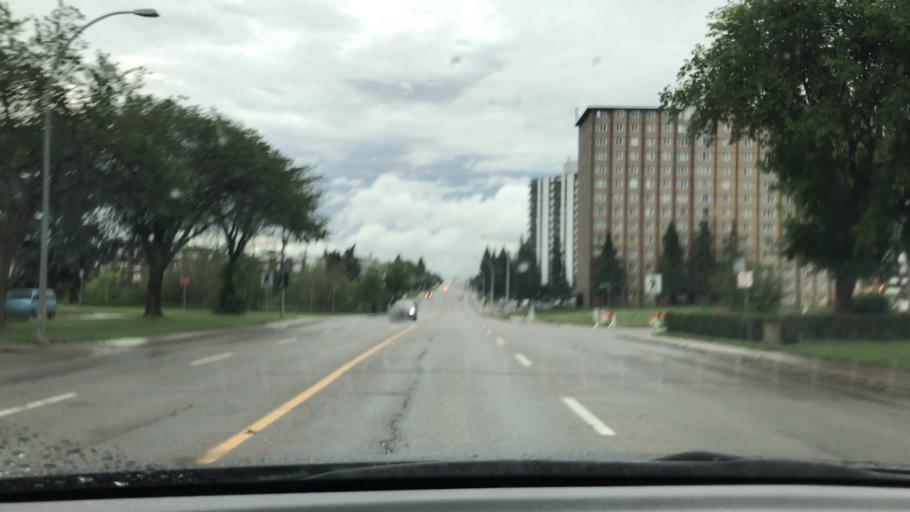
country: CA
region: Alberta
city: Edmonton
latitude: 53.5412
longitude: -113.4335
